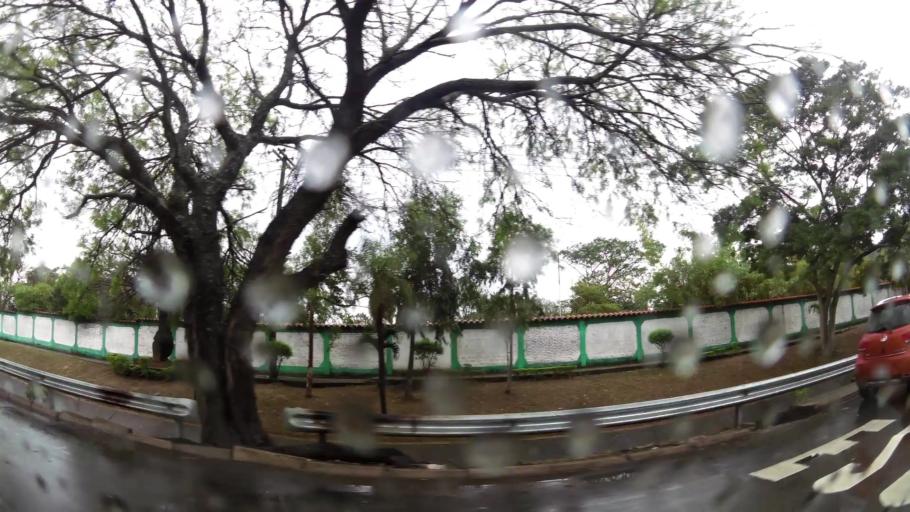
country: BO
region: Santa Cruz
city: Santa Cruz de la Sierra
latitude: -17.8015
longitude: -63.2030
